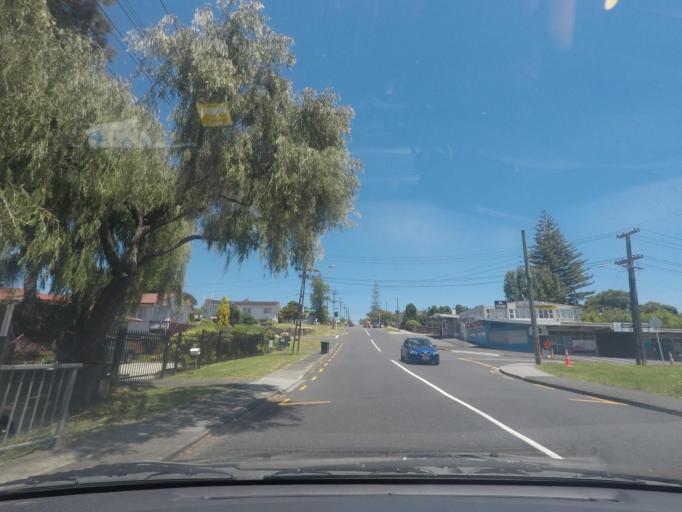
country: NZ
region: Auckland
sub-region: Auckland
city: Waitakere
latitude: -36.9134
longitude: 174.7164
